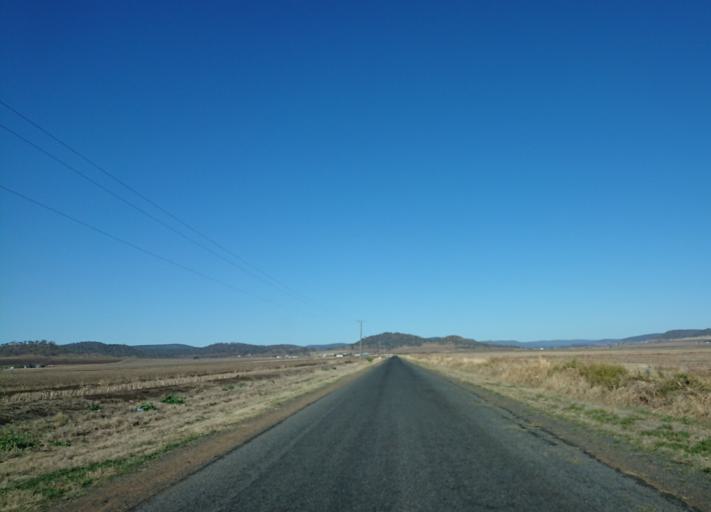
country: AU
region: Queensland
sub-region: Toowoomba
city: Top Camp
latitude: -27.8152
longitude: 151.9883
